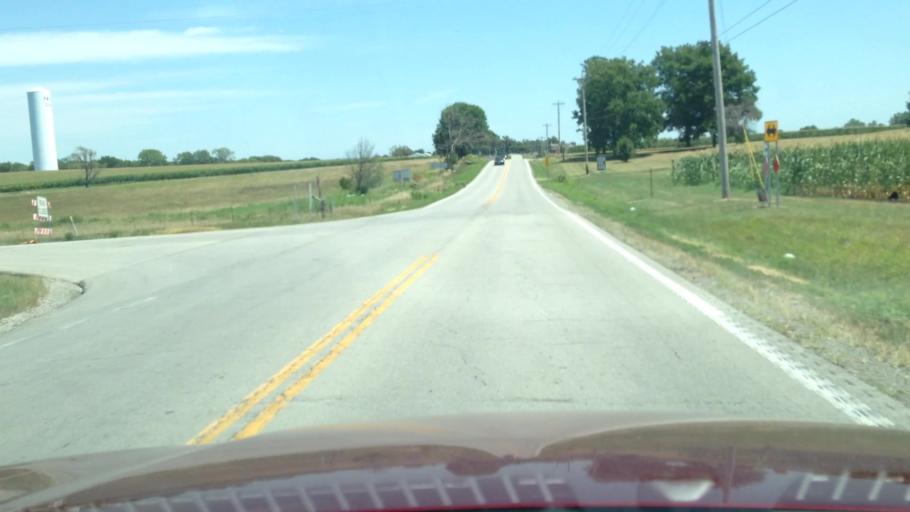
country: US
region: Missouri
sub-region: Clay County
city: Kearney
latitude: 39.3678
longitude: -94.4455
